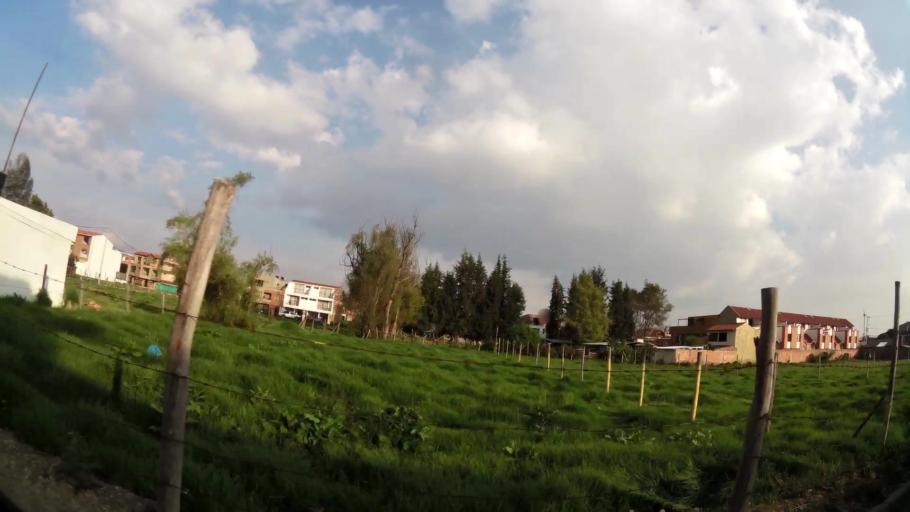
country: CO
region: Cundinamarca
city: Cota
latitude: 4.8124
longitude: -74.1051
